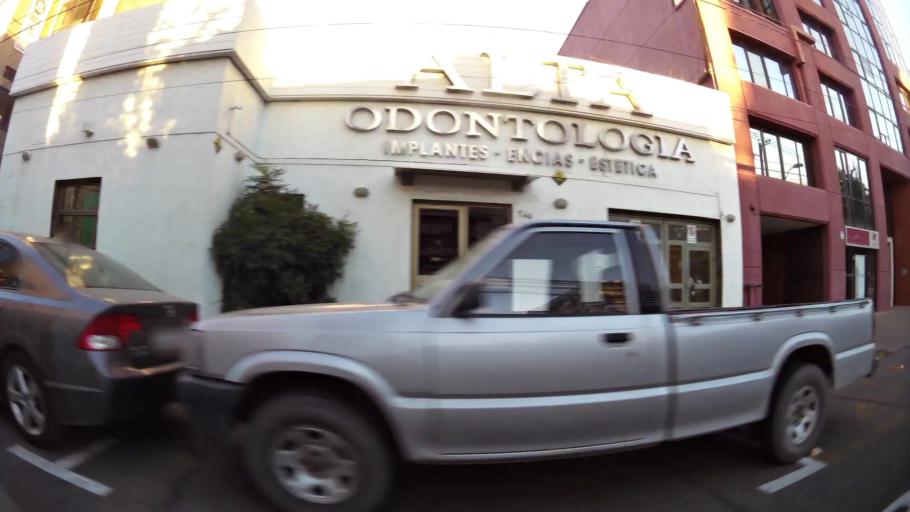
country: CL
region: Maule
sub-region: Provincia de Curico
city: Curico
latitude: -34.9829
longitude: -71.2390
